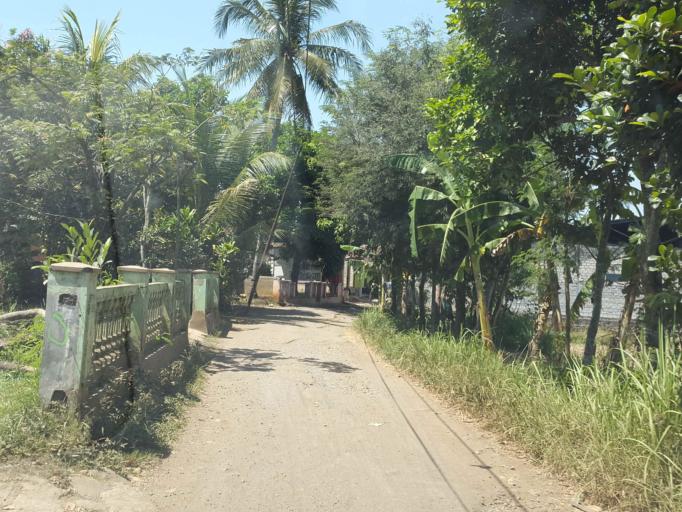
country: ID
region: West Java
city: Ciranjang-hilir
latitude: -6.7885
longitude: 107.2767
